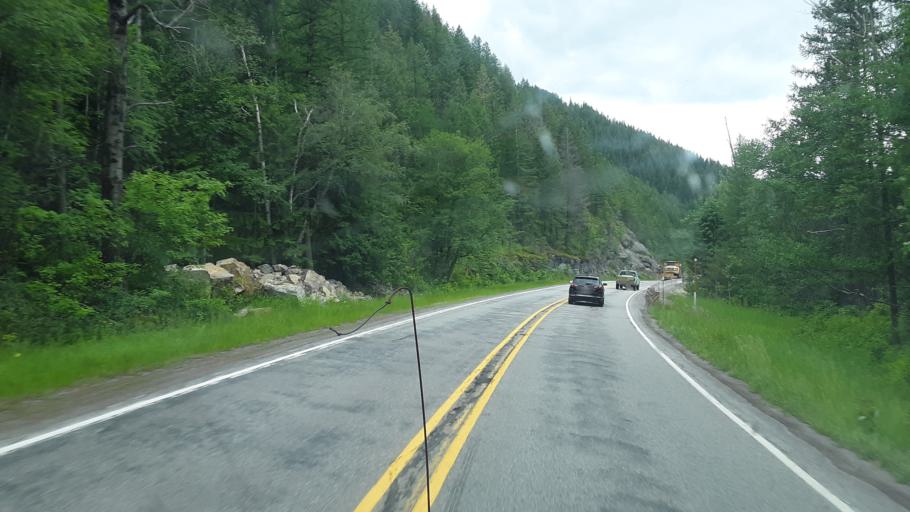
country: US
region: Montana
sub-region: Flathead County
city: Columbia Falls
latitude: 48.4923
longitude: -113.9090
